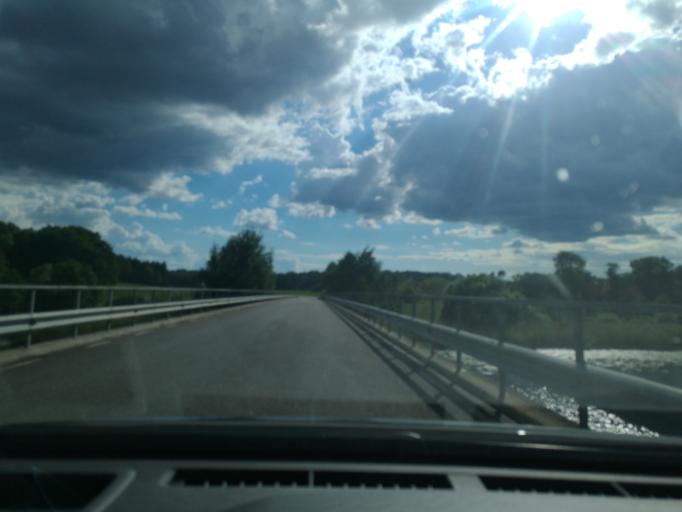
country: SE
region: Soedermanland
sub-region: Eskilstuna Kommun
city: Arla
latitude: 59.4523
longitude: 16.7287
